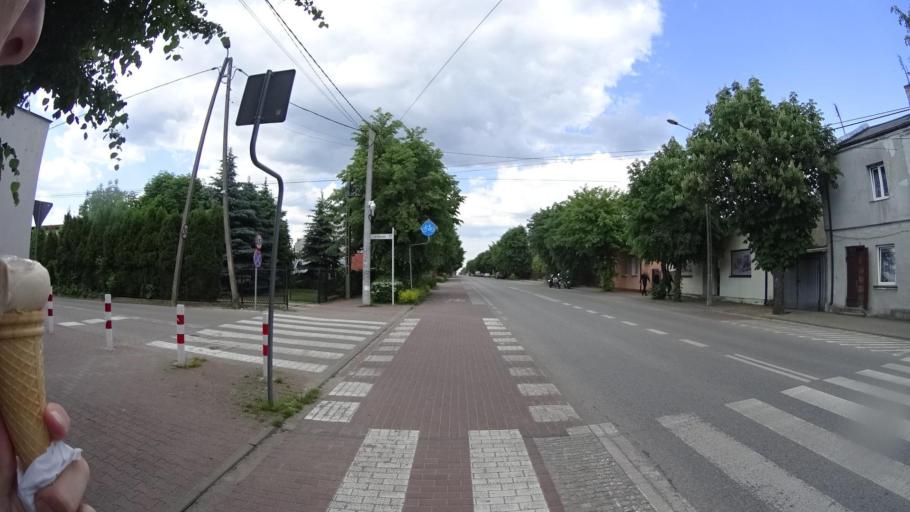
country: PL
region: Masovian Voivodeship
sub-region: Powiat piaseczynski
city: Tarczyn
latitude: 51.9822
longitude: 20.8343
